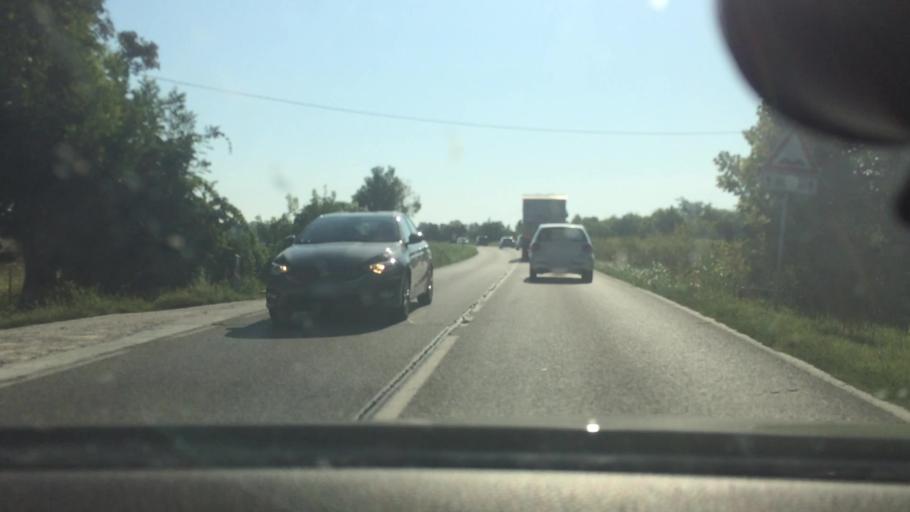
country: IT
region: Emilia-Romagna
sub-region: Provincia di Ferrara
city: Porto Garibaldi
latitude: 44.6889
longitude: 12.2117
